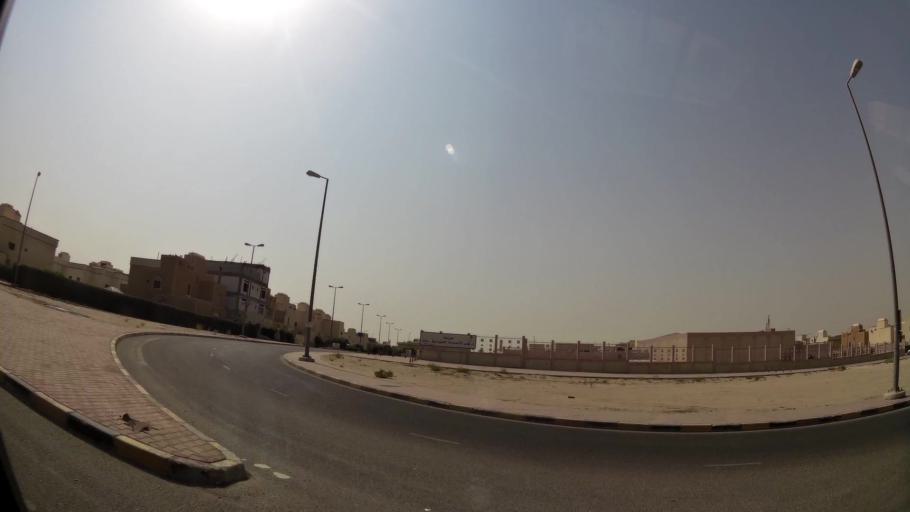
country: KW
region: Muhafazat al Jahra'
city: Al Jahra'
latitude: 29.3201
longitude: 47.7367
